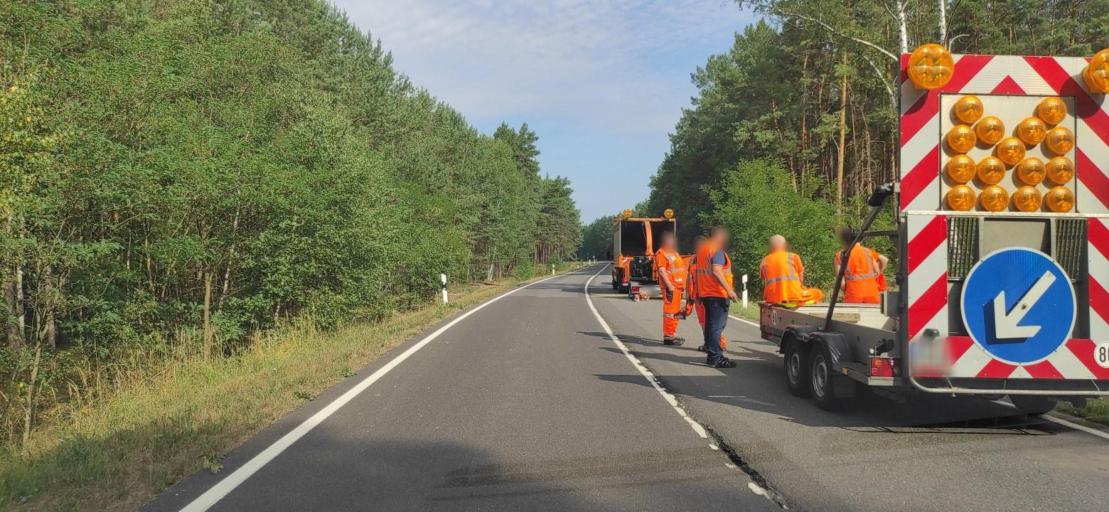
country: PL
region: Lubusz
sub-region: Powiat zarski
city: Trzebiel
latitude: 51.6755
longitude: 14.7296
